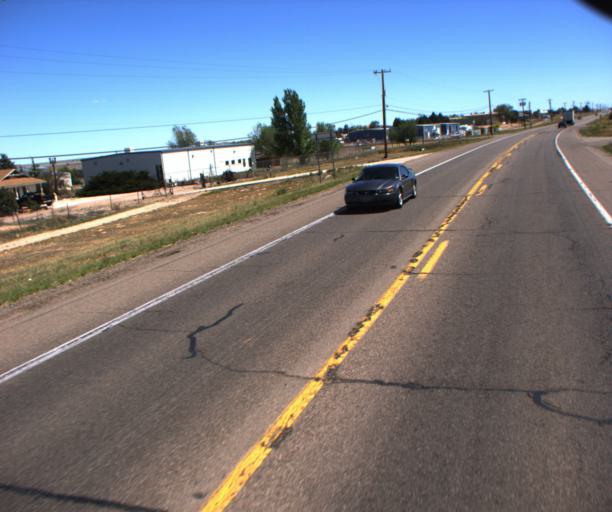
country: US
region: Arizona
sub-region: Yavapai County
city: Chino Valley
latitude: 34.8038
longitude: -112.4502
